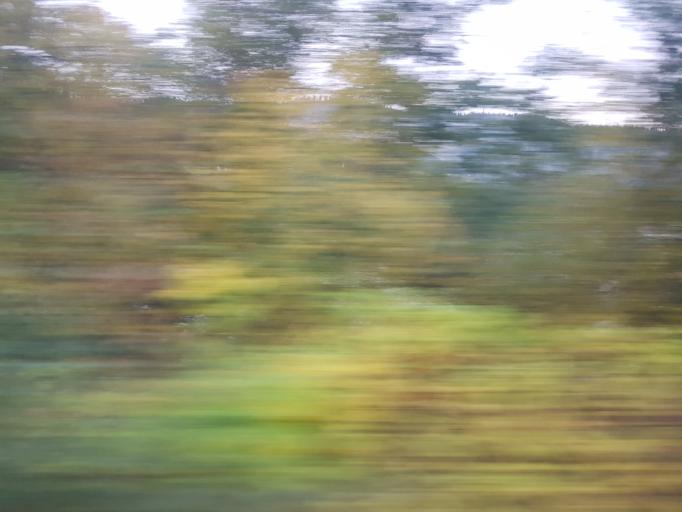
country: NO
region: Sor-Trondelag
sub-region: Melhus
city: Lundamo
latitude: 63.1126
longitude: 10.2379
